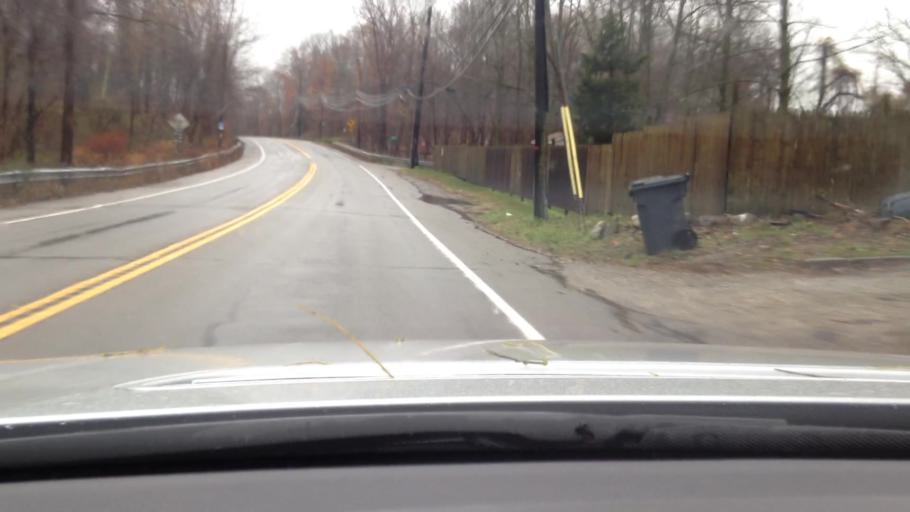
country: US
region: New York
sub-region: Westchester County
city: Peekskill
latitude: 41.3190
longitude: -73.9304
